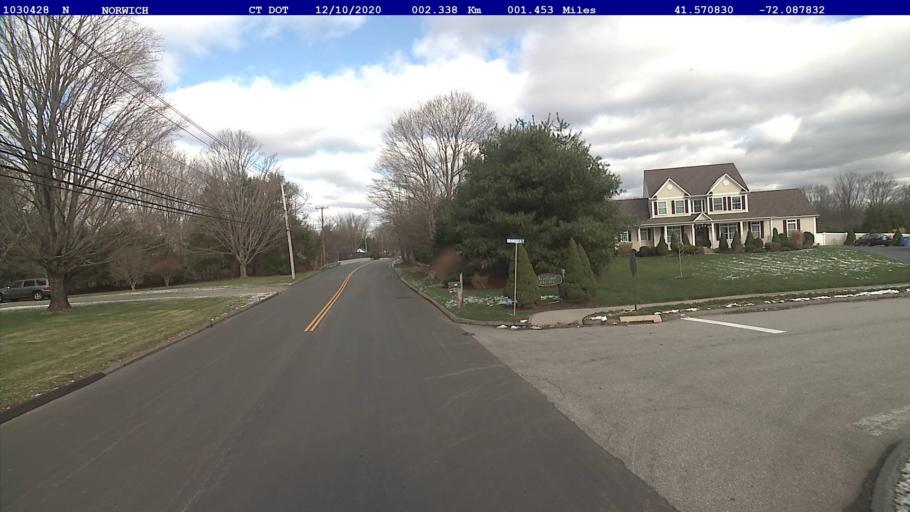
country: US
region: Connecticut
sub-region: New London County
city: Baltic
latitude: 41.5708
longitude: -72.0878
